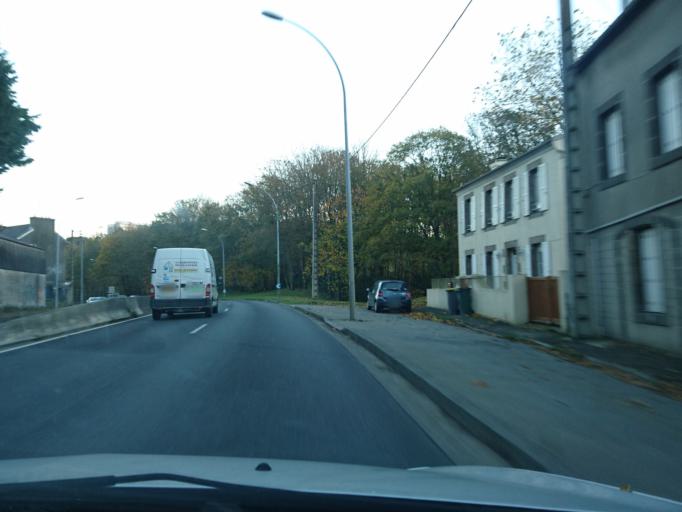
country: FR
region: Brittany
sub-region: Departement du Finistere
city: Bohars
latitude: 48.4106
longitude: -4.5260
